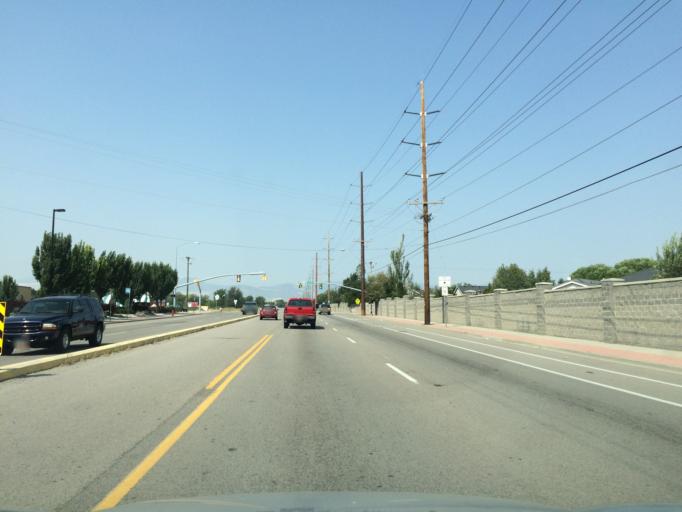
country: US
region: Utah
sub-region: Salt Lake County
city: West Jordan
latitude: 40.5878
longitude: -111.9468
